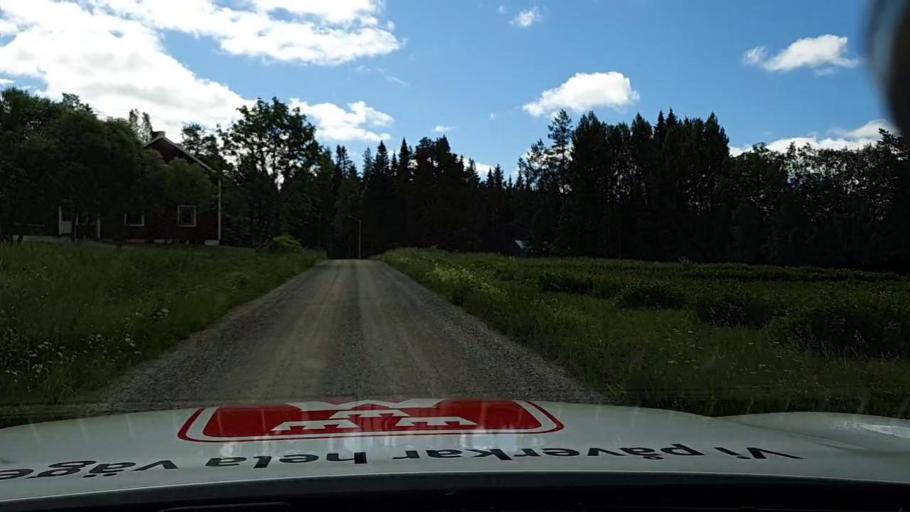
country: SE
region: Jaemtland
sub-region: Braecke Kommun
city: Braecke
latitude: 62.7592
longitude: 15.5000
